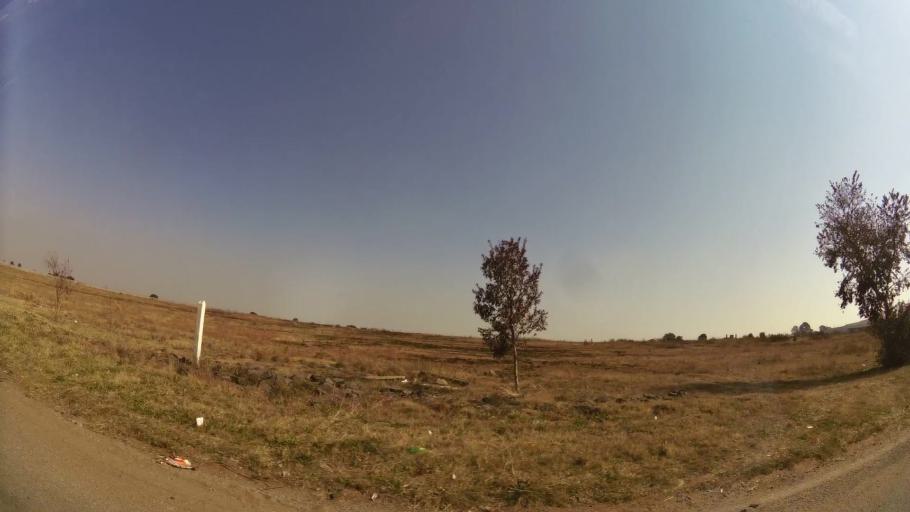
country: ZA
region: Gauteng
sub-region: Ekurhuleni Metropolitan Municipality
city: Boksburg
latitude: -26.2349
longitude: 28.2956
